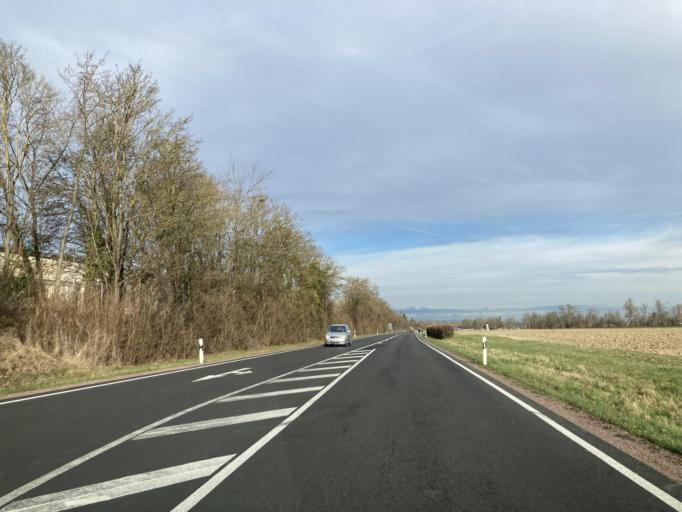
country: DE
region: Baden-Wuerttemberg
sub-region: Freiburg Region
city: Breisach am Rhein
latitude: 48.0354
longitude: 7.5926
